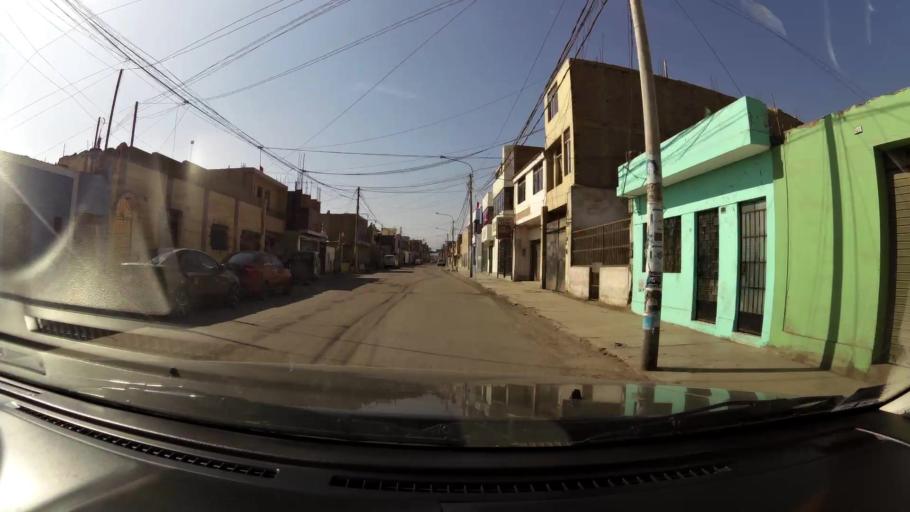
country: PE
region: Ica
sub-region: Provincia de Chincha
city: Chincha Alta
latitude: -13.4229
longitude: -76.1336
